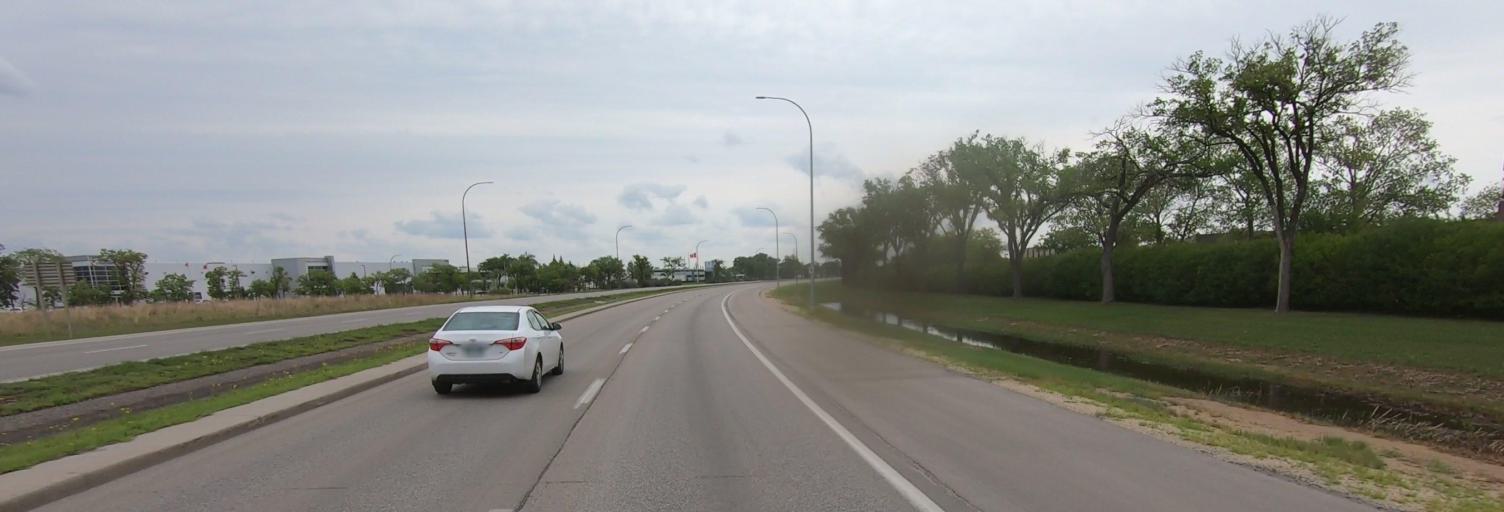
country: CA
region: Manitoba
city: Winnipeg
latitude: 49.8327
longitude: -97.1773
